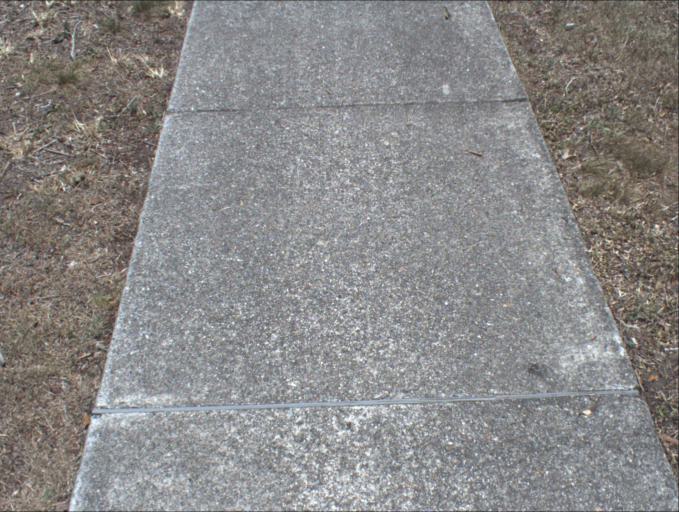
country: AU
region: Queensland
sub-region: Logan
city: Windaroo
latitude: -27.7330
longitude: 153.2085
